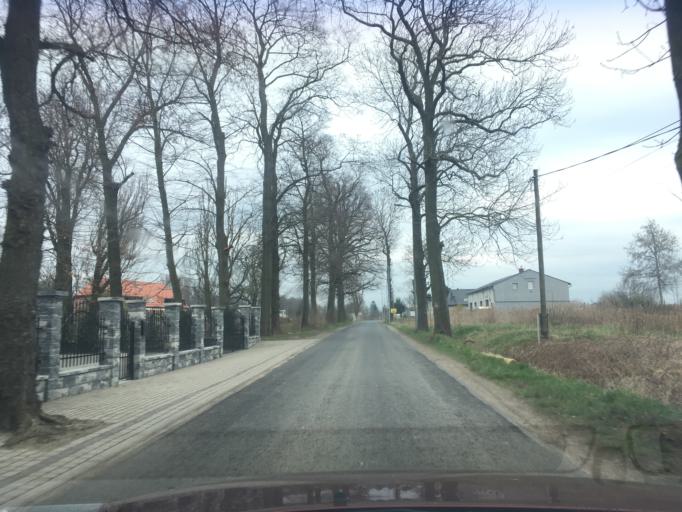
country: PL
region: Lower Silesian Voivodeship
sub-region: Powiat zgorzelecki
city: Lagow
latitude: 51.1660
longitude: 15.0380
